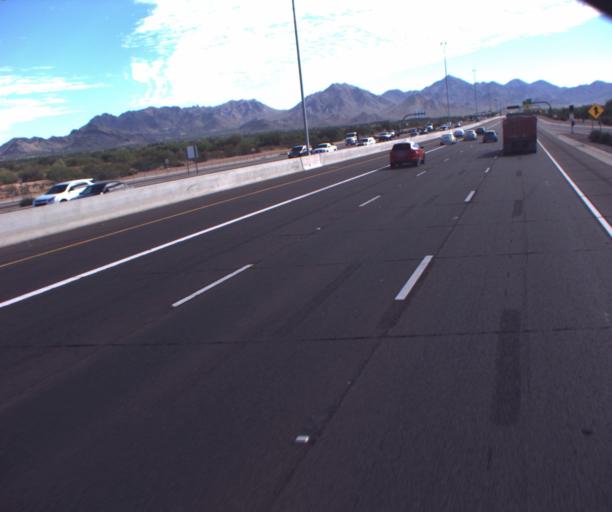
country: US
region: Arizona
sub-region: Maricopa County
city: Paradise Valley
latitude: 33.6573
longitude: -111.9218
